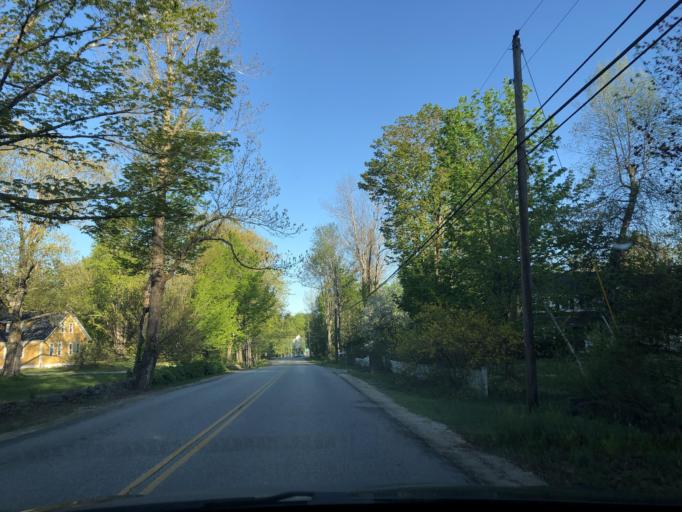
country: US
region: New Hampshire
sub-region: Merrimack County
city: New London
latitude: 43.4229
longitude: -72.0311
